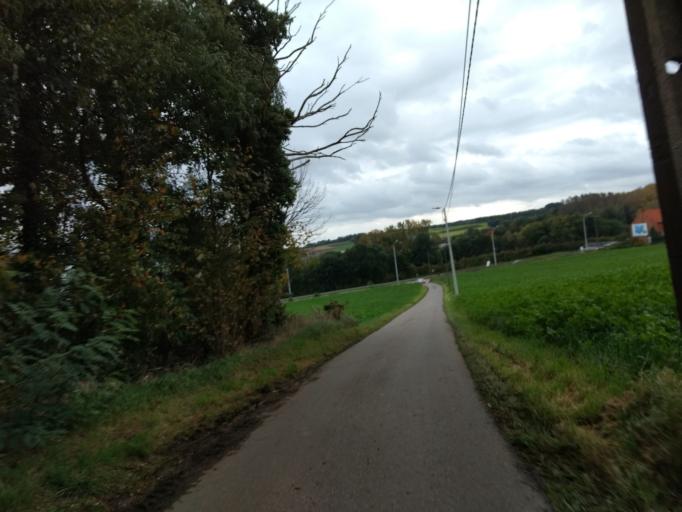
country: BE
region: Flanders
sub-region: Provincie Vlaams-Brabant
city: Bekkevoort
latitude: 50.9587
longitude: 5.0119
